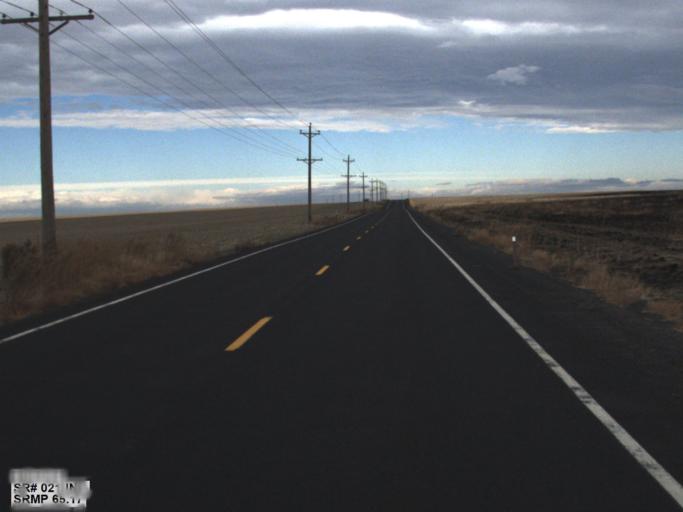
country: US
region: Washington
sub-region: Adams County
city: Ritzville
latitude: 47.4438
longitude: -118.7338
